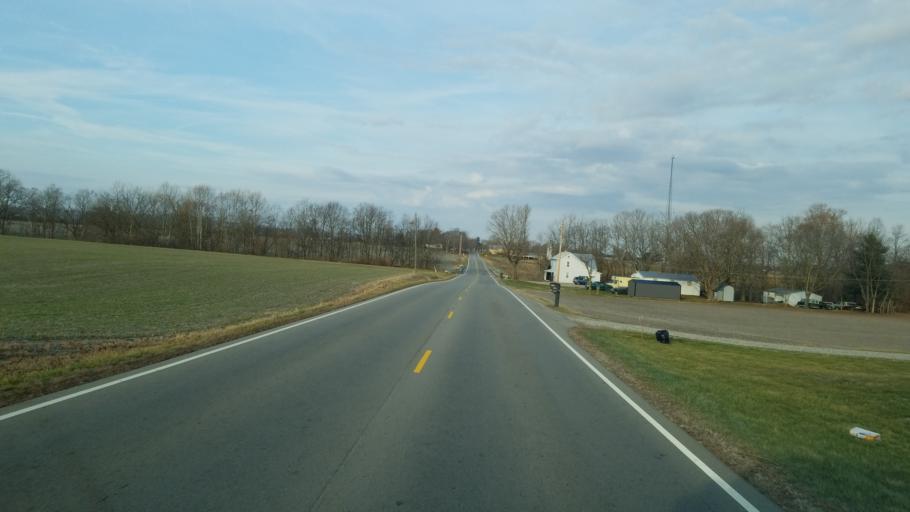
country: US
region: Ohio
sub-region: Ross County
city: Chillicothe
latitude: 39.2950
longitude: -82.8899
